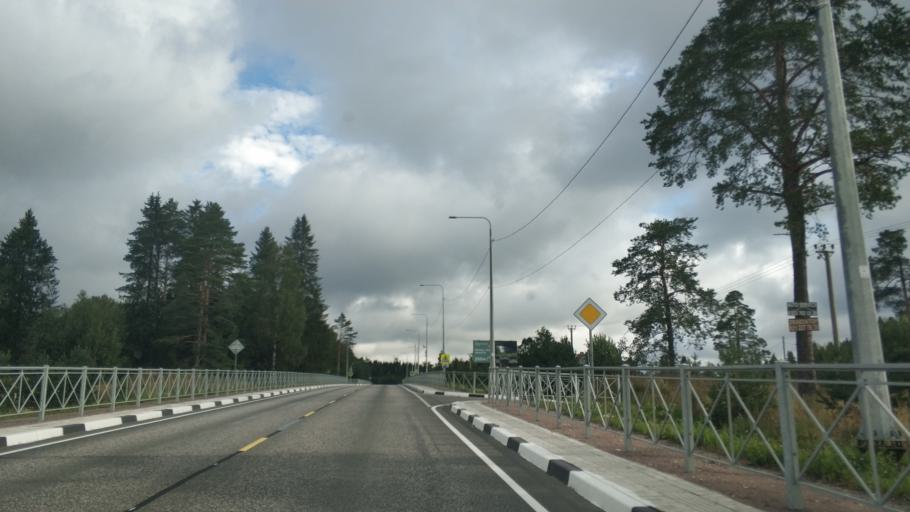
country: RU
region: Republic of Karelia
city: Khelyulya
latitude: 61.8202
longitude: 30.6334
